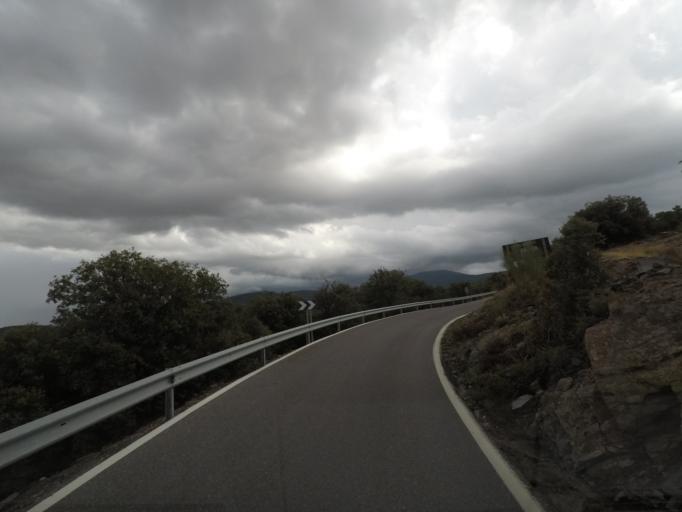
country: ES
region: Andalusia
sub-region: Provincia de Granada
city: Ferreira
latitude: 37.1591
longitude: -3.0511
